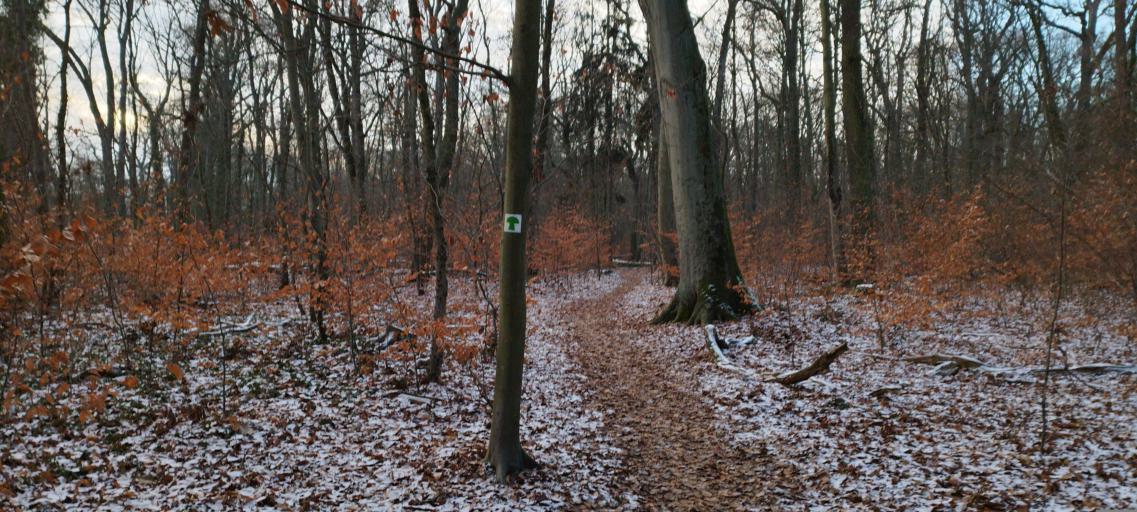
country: DE
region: Brandenburg
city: Konigs Wusterhausen
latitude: 52.2908
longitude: 13.6461
